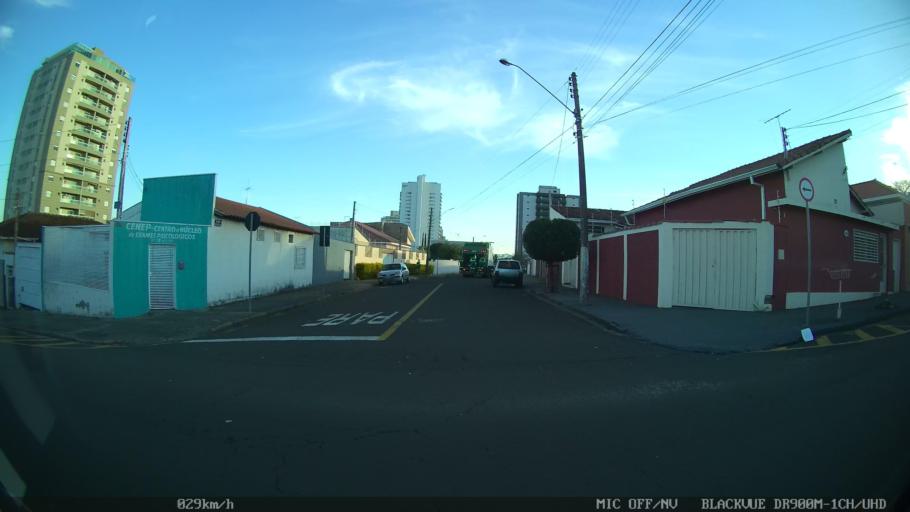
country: BR
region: Sao Paulo
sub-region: Franca
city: Franca
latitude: -20.5302
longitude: -47.3902
